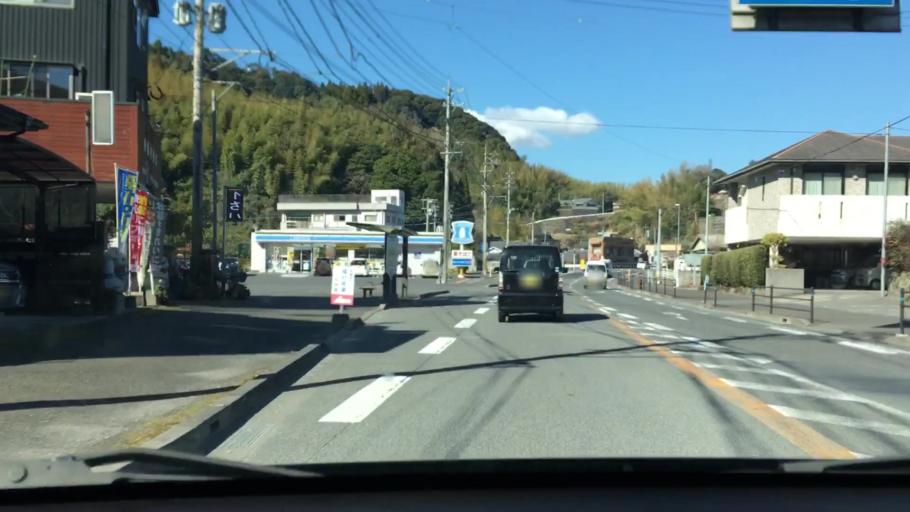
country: JP
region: Kagoshima
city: Ijuin
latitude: 31.6551
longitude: 130.4968
